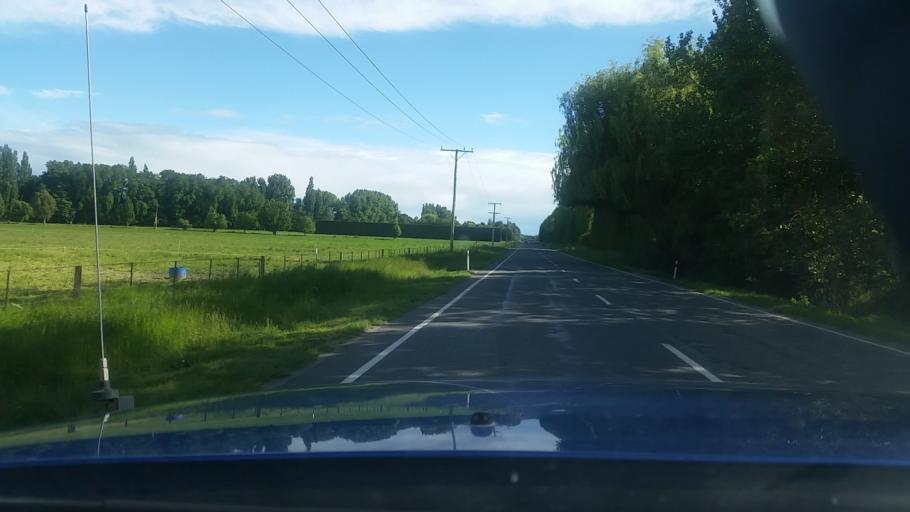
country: NZ
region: Canterbury
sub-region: Ashburton District
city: Ashburton
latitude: -43.8629
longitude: 171.7294
